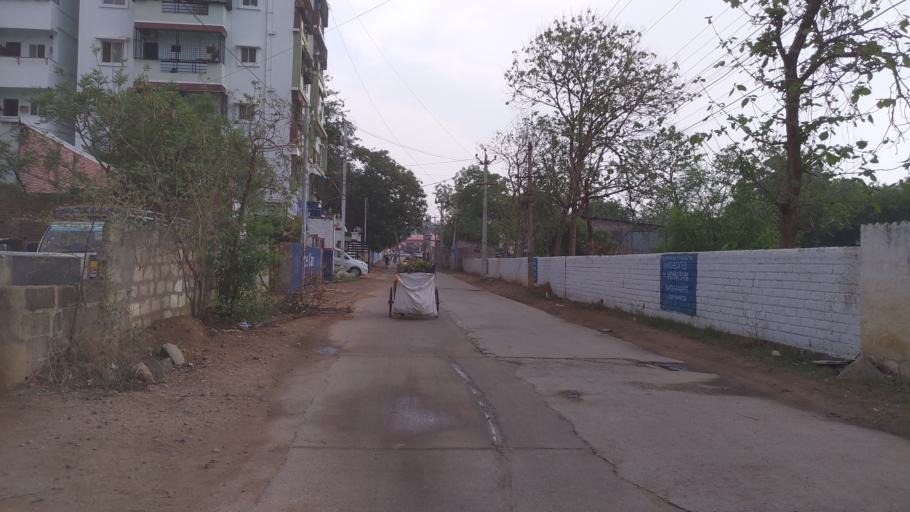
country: IN
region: Telangana
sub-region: Rangareddi
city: Lal Bahadur Nagar
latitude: 17.3347
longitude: 78.5781
